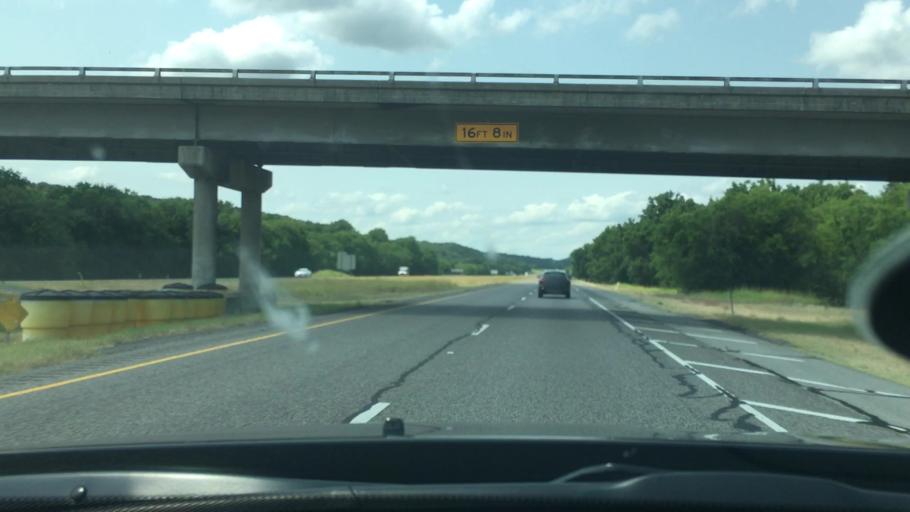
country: US
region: Oklahoma
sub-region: Murray County
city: Davis
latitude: 34.4548
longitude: -97.1390
